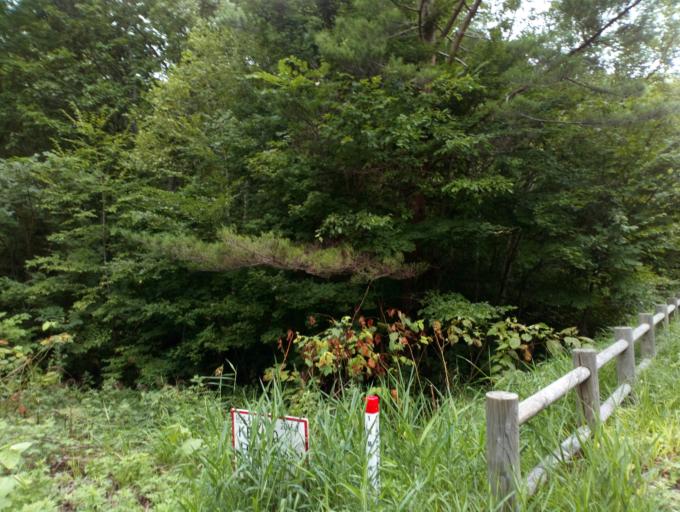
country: JP
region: Hokkaido
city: Nanae
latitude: 42.0053
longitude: 140.6911
